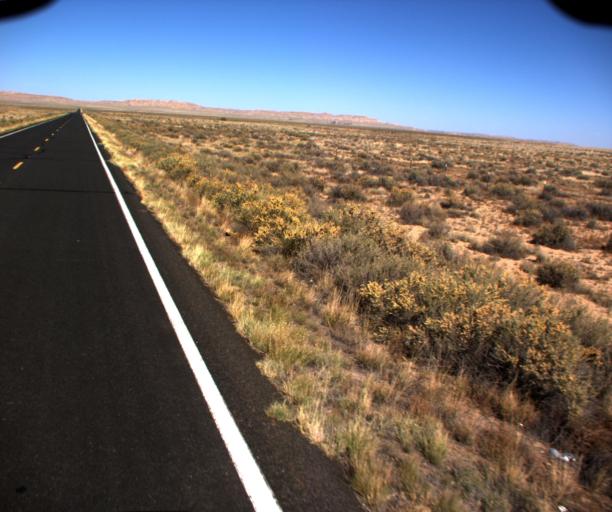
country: US
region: Arizona
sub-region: Navajo County
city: First Mesa
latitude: 35.7031
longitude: -110.5085
